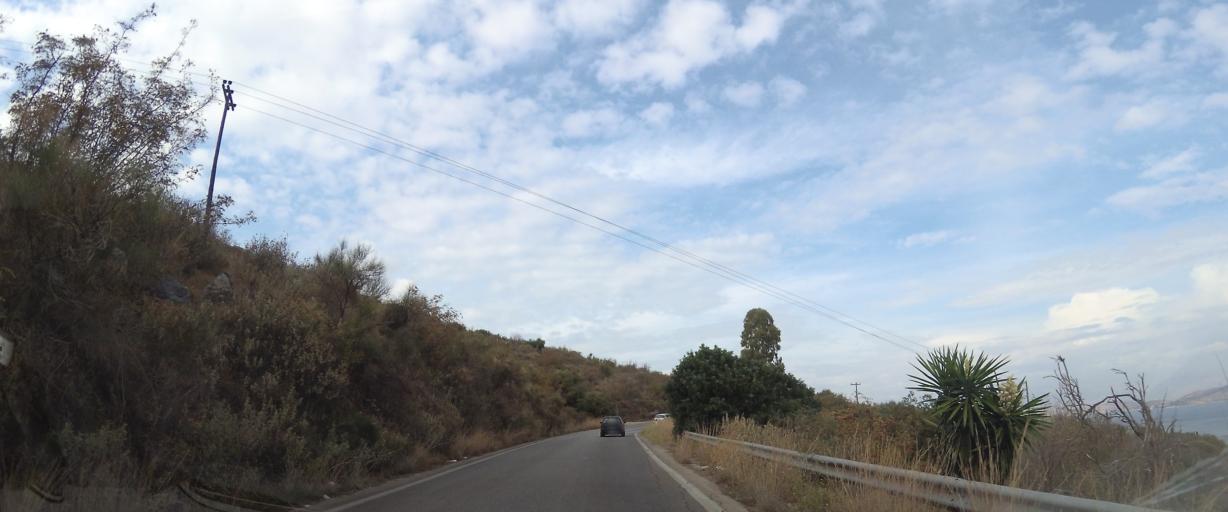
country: AL
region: Vlore
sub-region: Rrethi i Sarandes
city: Xarre
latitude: 39.7486
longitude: 19.9384
